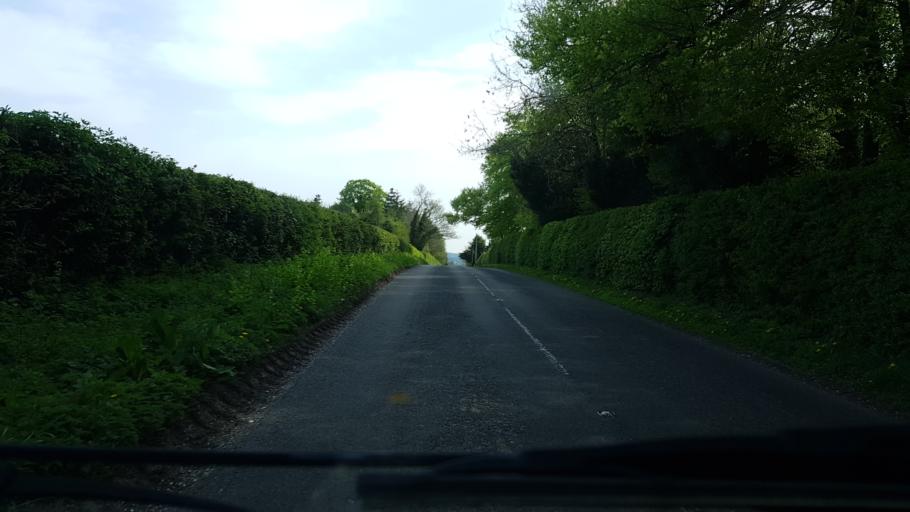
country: GB
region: England
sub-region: Hampshire
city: Overton
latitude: 51.2751
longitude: -1.2632
